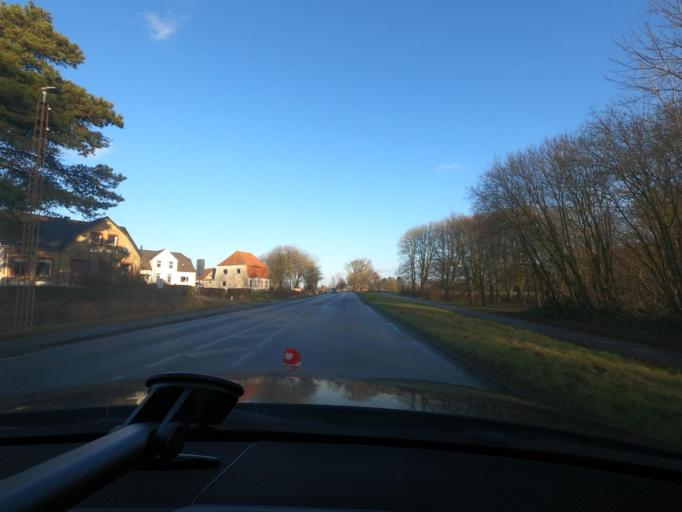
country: DK
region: South Denmark
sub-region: Sonderborg Kommune
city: Grasten
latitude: 54.9046
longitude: 9.5742
